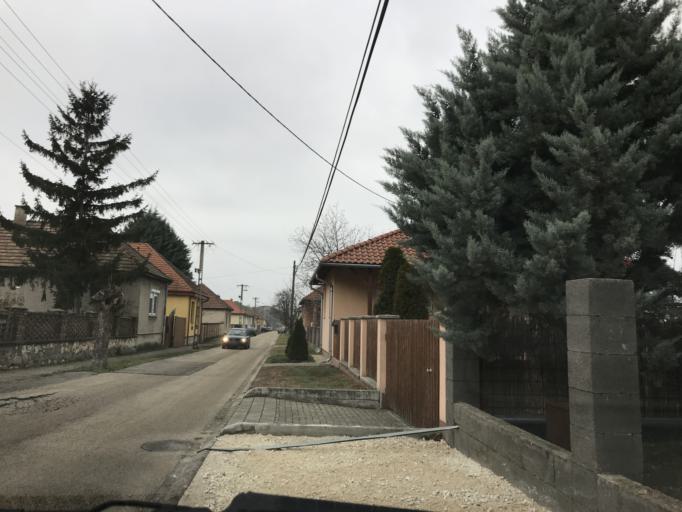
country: HU
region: Komarom-Esztergom
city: Tokod
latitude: 47.7277
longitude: 18.6645
